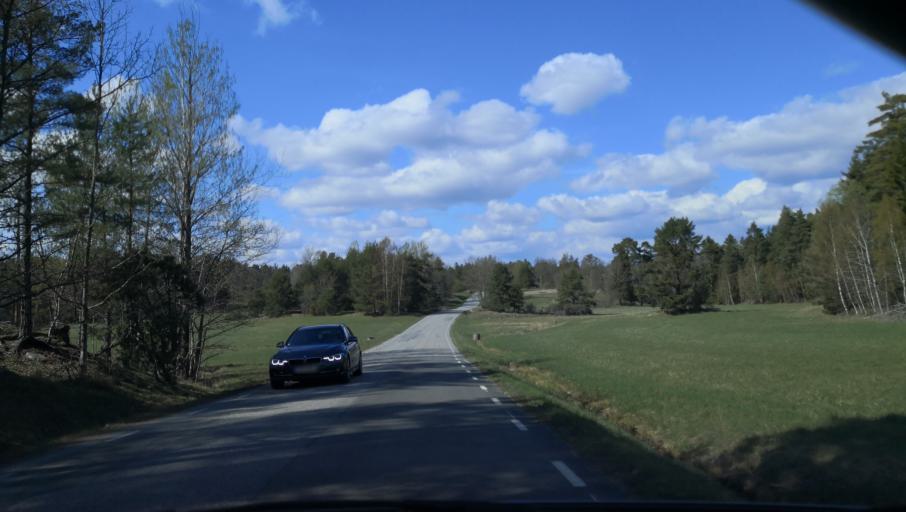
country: SE
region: Stockholm
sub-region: Varmdo Kommun
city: Hemmesta
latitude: 59.4038
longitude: 18.5069
